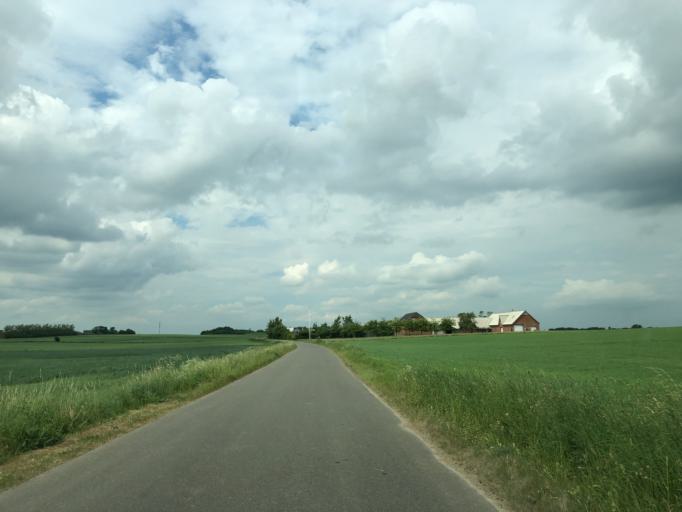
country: DK
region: Central Jutland
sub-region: Struer Kommune
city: Struer
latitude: 56.4658
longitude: 8.5766
